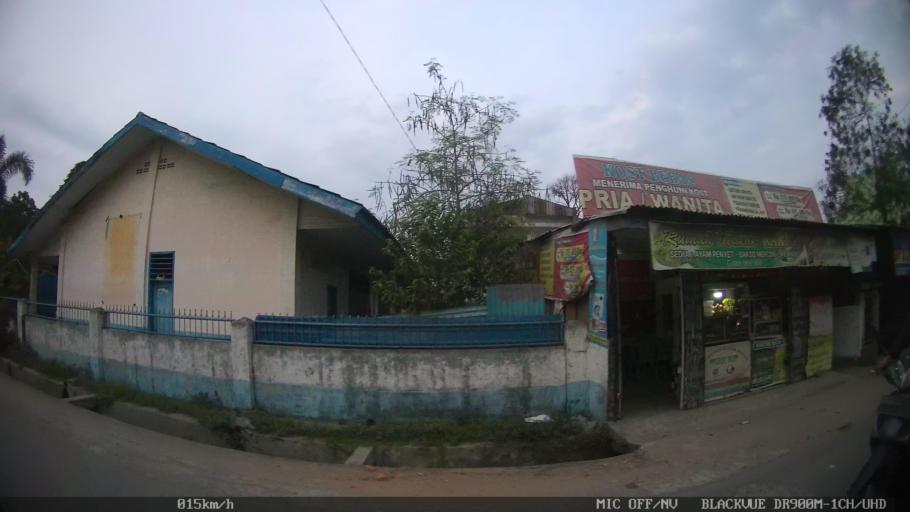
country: ID
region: North Sumatra
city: Sunggal
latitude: 3.5967
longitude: 98.6029
